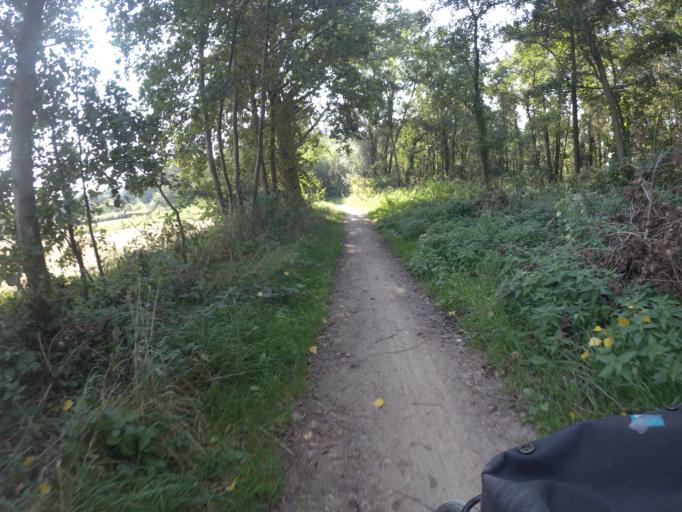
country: NL
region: North Brabant
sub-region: Gemeente Schijndel
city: Schijndel
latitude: 51.6510
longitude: 5.4467
